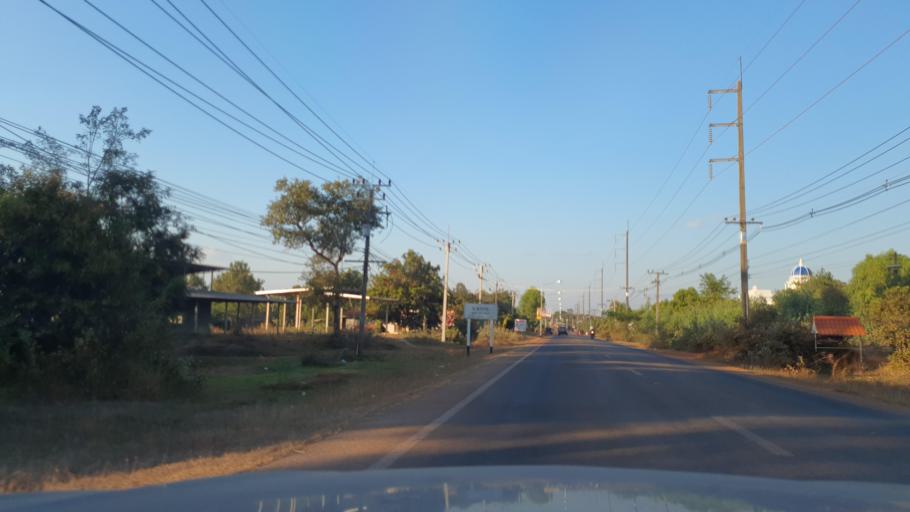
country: TH
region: Nakhon Phanom
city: Si Songkhram
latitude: 17.5804
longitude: 104.2329
